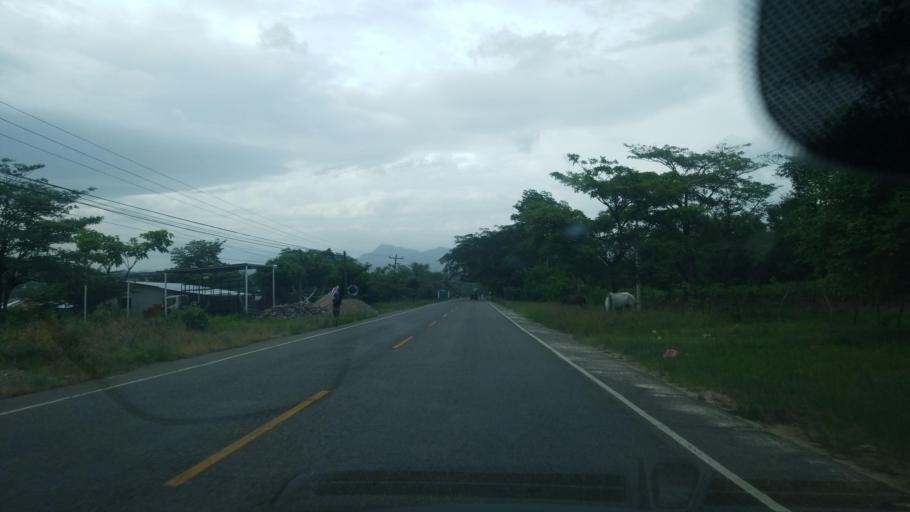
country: HN
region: Ocotepeque
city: Antigua Ocotepeque
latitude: 14.4066
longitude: -89.1955
